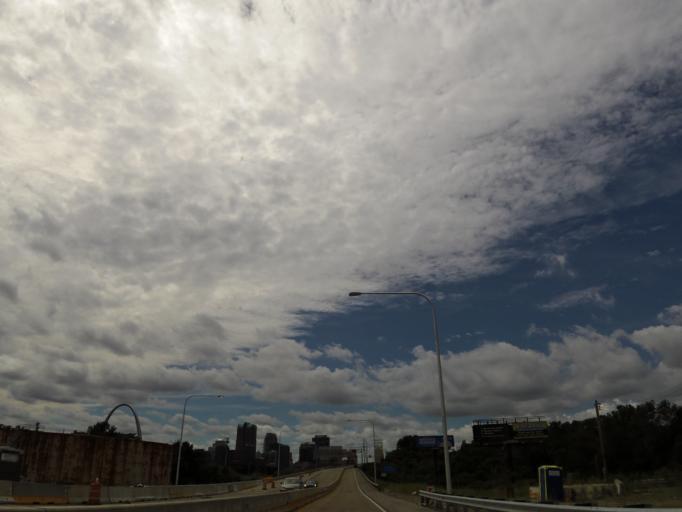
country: US
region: Illinois
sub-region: Saint Clair County
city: East Saint Louis
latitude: 38.6301
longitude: -90.1677
